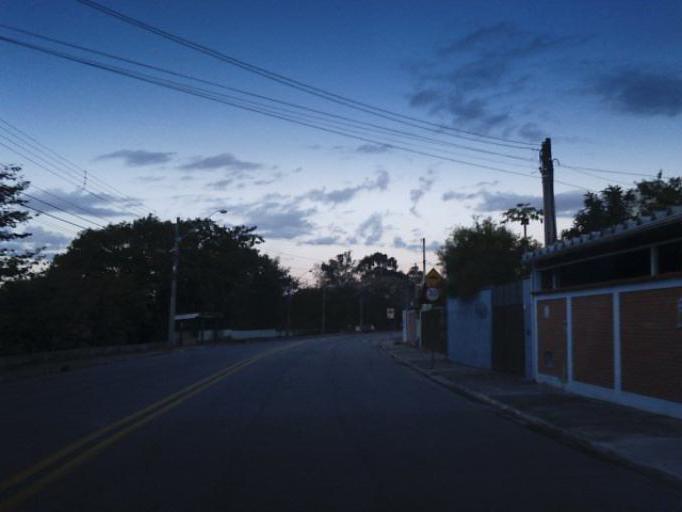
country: BR
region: Sao Paulo
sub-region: Sao Jose Dos Campos
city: Sao Jose dos Campos
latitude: -23.2099
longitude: -45.8548
